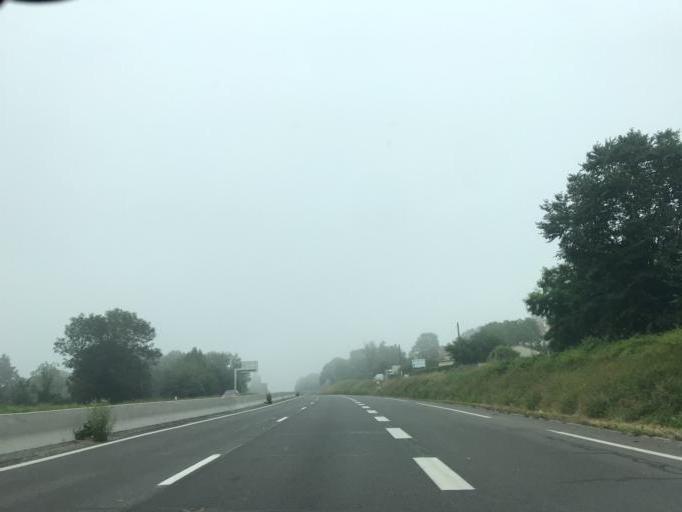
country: FR
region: Ile-de-France
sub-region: Departement de Seine-et-Marne
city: Saint-Thibault-des-Vignes
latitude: 48.8660
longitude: 2.6836
